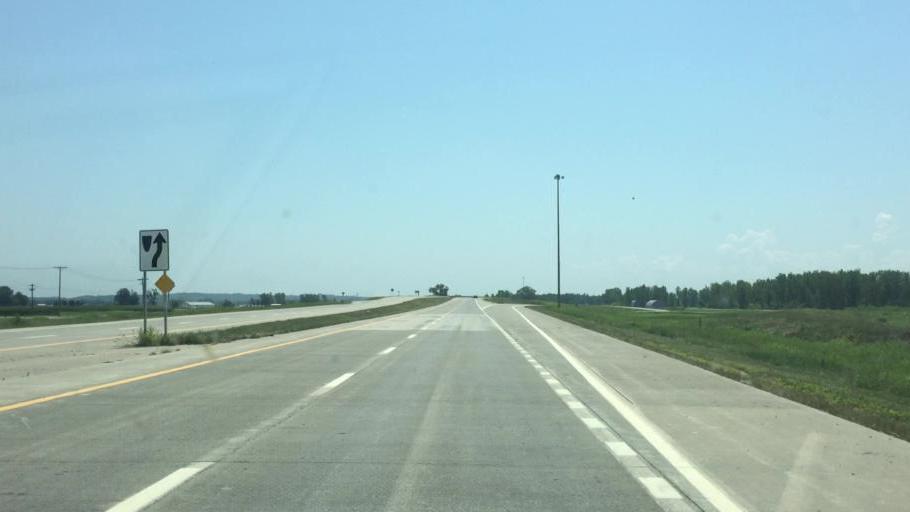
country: US
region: Kansas
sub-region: Doniphan County
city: Wathena
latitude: 39.7505
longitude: -94.9300
